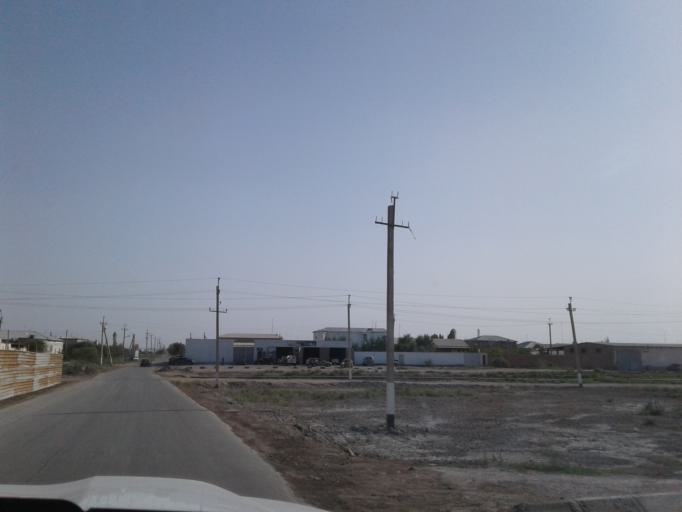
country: TM
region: Dasoguz
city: Dasoguz
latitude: 41.8508
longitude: 59.9238
